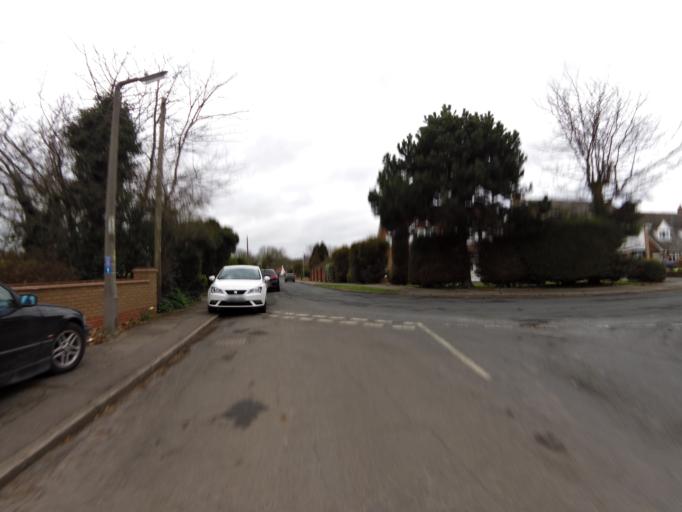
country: GB
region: England
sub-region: Norfolk
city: Hopton on Sea
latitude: 52.5079
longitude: 1.7362
